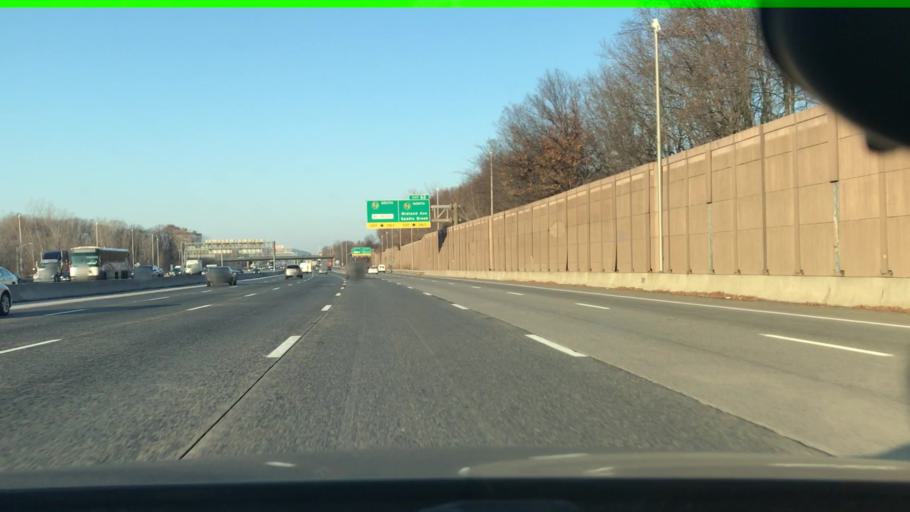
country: US
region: New Jersey
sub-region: Bergen County
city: Saddle Brook
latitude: 40.9032
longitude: -74.0918
